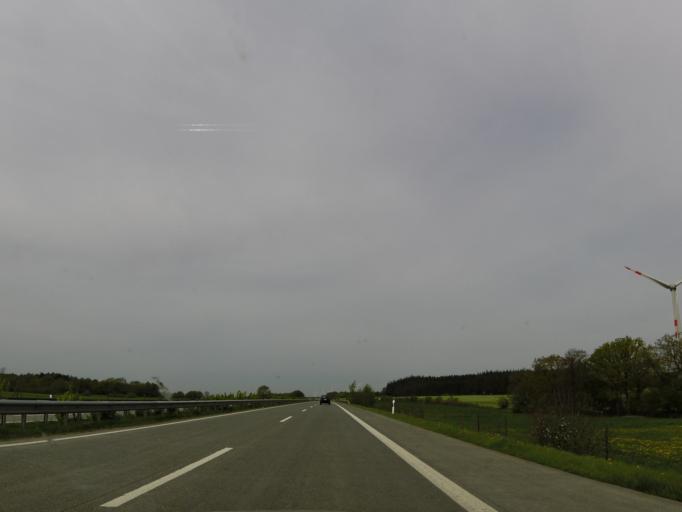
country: DE
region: Schleswig-Holstein
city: Nienbuttel
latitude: 54.0402
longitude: 9.4198
